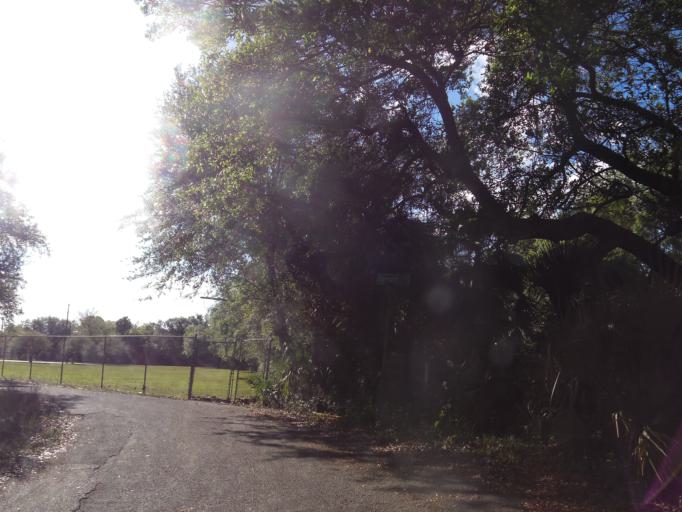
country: US
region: Florida
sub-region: Duval County
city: Jacksonville
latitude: 30.3264
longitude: -81.6734
